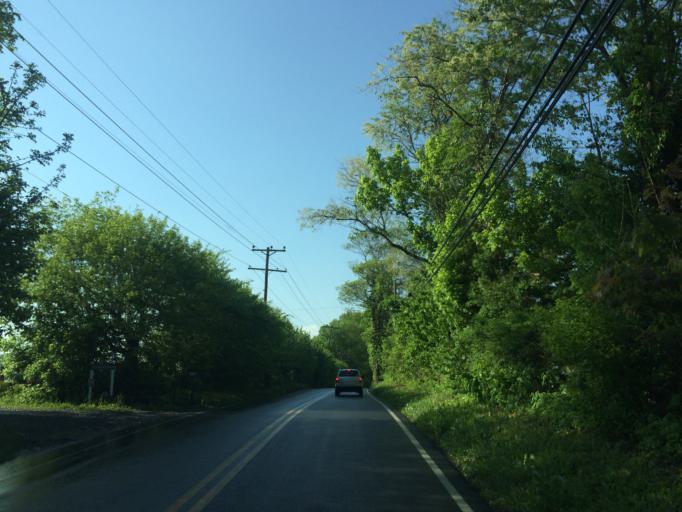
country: US
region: Maryland
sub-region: Howard County
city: Highland
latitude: 39.2412
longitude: -76.9426
